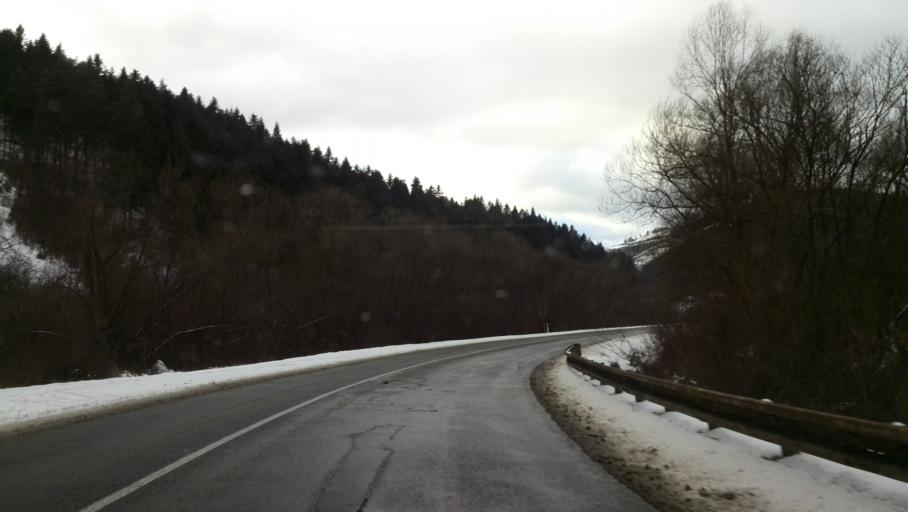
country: SK
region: Kosicky
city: Gelnica
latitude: 48.8667
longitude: 20.9749
